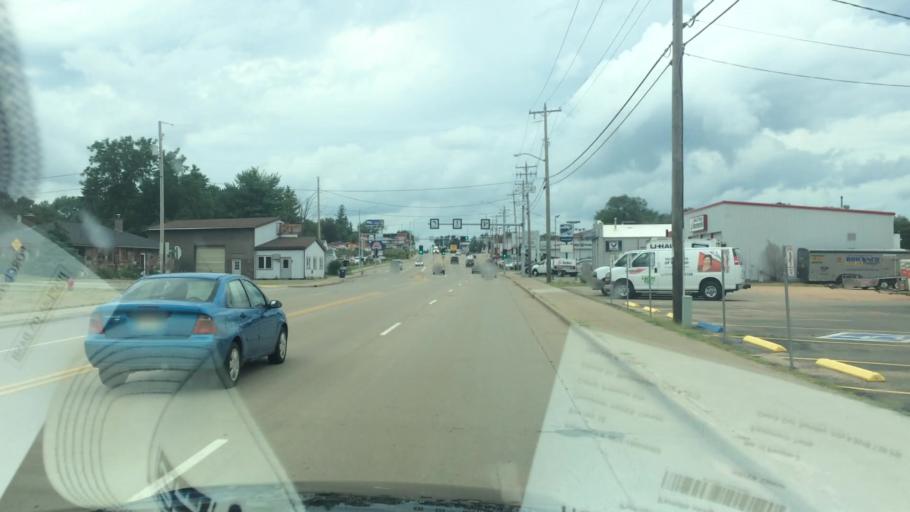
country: US
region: Wisconsin
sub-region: Marathon County
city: Schofield
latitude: 44.9294
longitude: -89.6142
